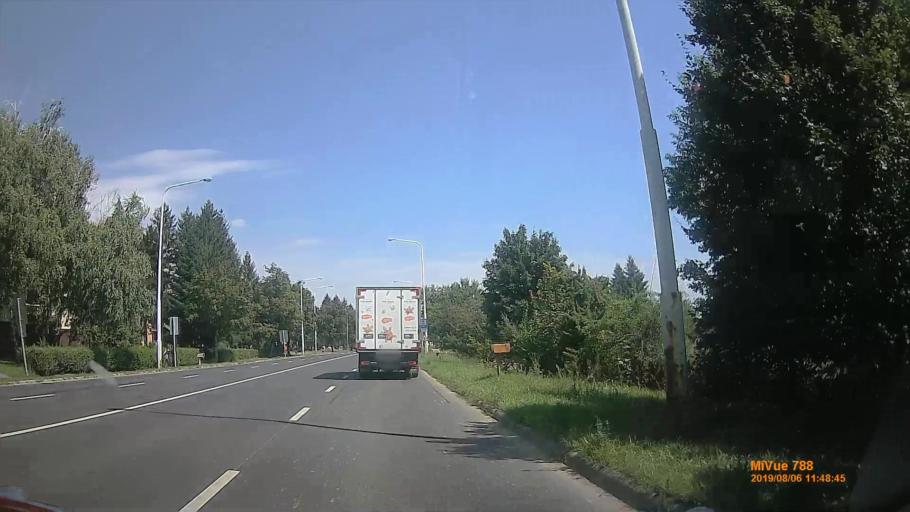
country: HU
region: Vas
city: Kormend
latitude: 47.0153
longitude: 16.6111
